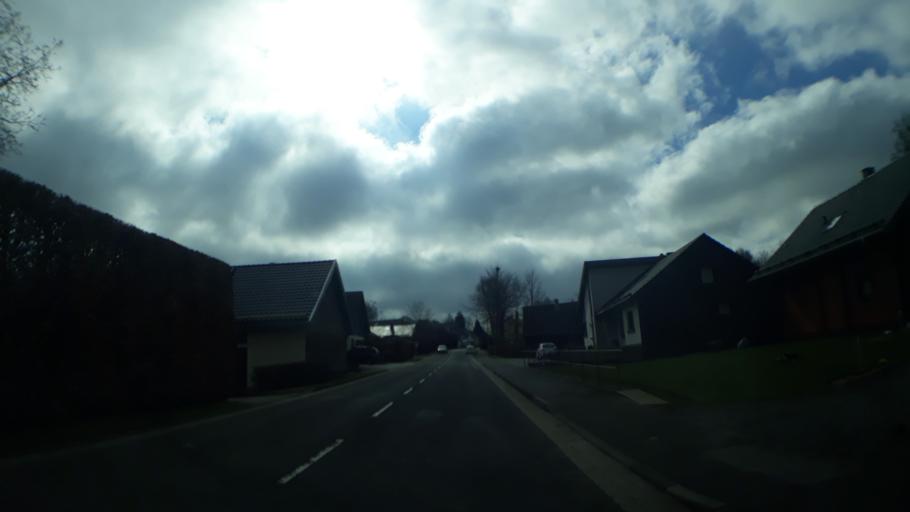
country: DE
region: North Rhine-Westphalia
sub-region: Regierungsbezirk Koln
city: Monschau
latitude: 50.5146
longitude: 6.2205
